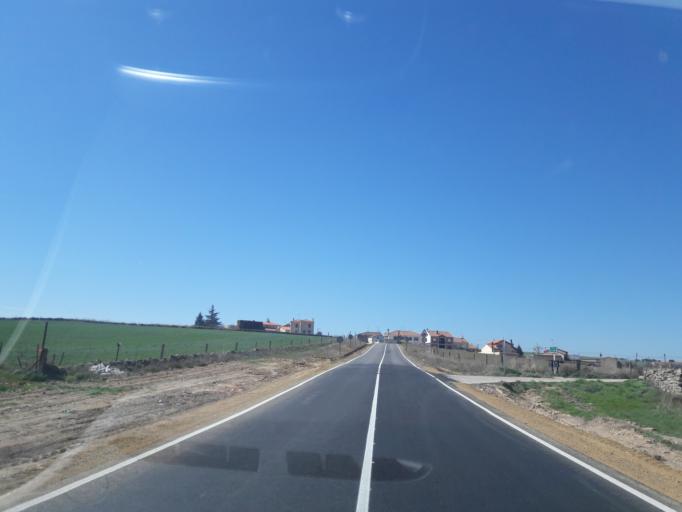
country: ES
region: Castille and Leon
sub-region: Provincia de Salamanca
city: Valdemierque
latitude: 40.8237
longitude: -5.5781
